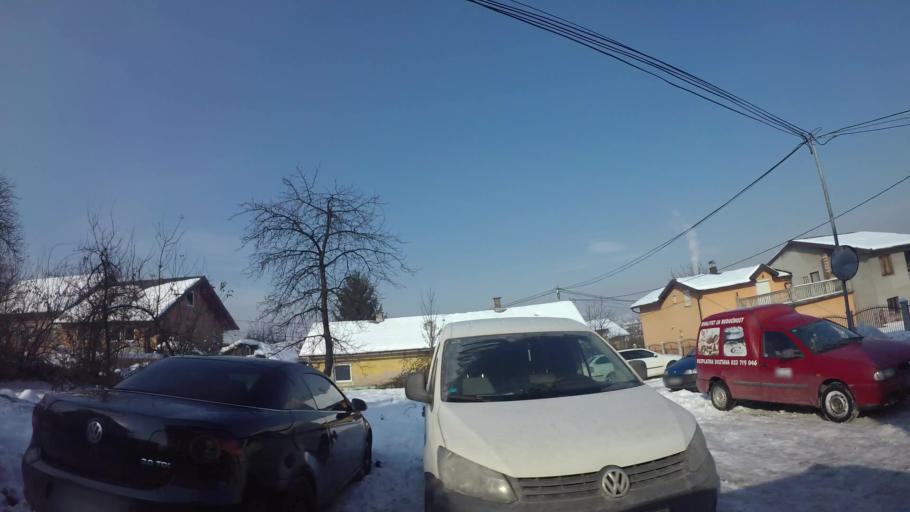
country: BA
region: Federation of Bosnia and Herzegovina
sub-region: Kanton Sarajevo
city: Sarajevo
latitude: 43.8426
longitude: 18.3646
